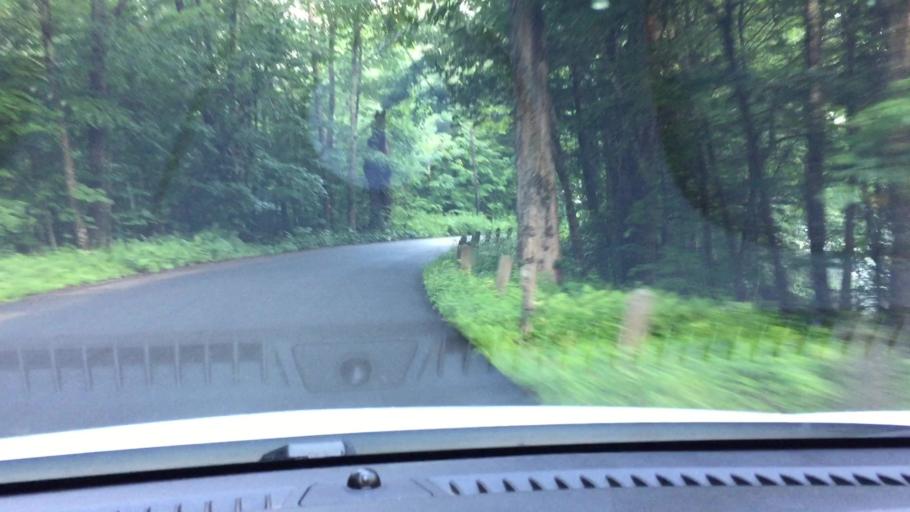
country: US
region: Massachusetts
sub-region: Hampshire County
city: Chesterfield
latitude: 42.3390
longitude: -72.9462
